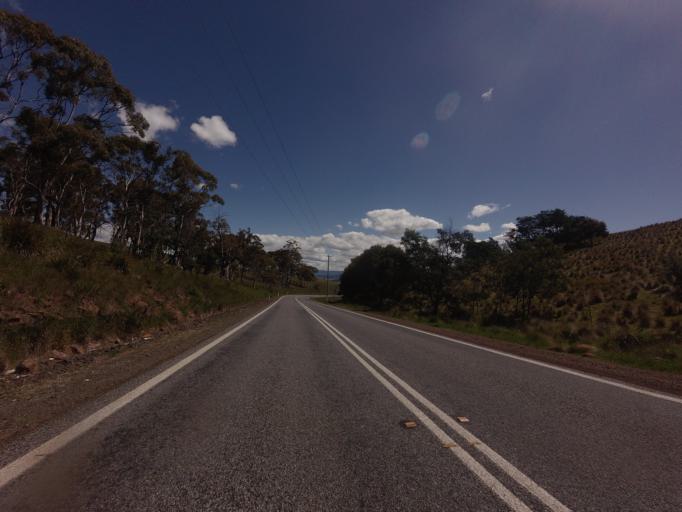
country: AU
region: Tasmania
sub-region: Northern Midlands
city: Evandale
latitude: -41.9408
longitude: 147.5947
